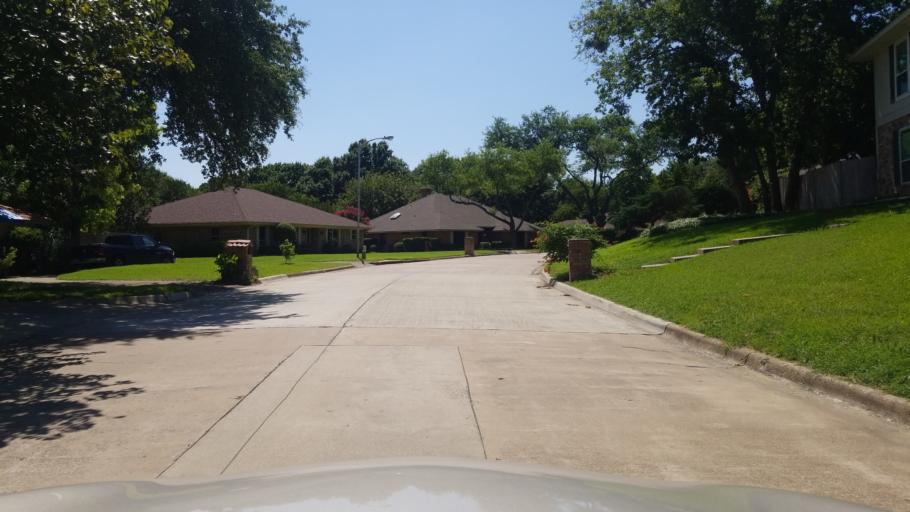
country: US
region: Texas
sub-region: Dallas County
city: Grand Prairie
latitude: 32.6890
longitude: -96.9991
